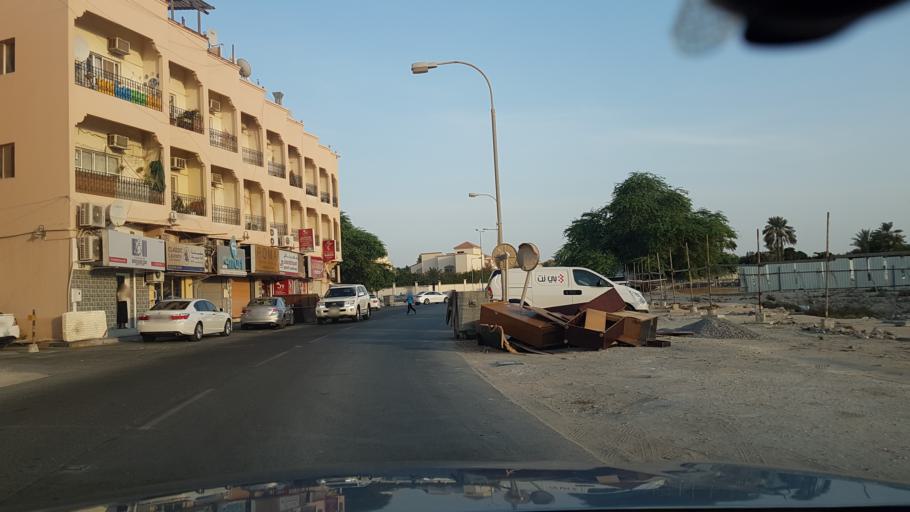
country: BH
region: Manama
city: Jidd Hafs
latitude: 26.2172
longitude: 50.4730
